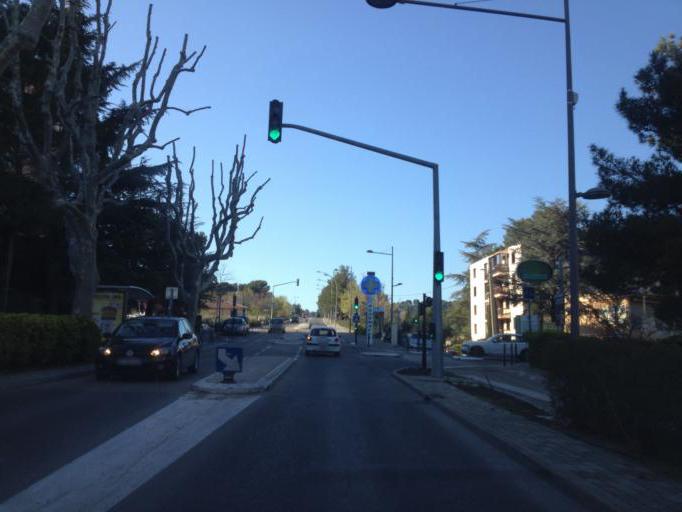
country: FR
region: Provence-Alpes-Cote d'Azur
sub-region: Departement des Bouches-du-Rhone
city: Aix-en-Provence
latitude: 43.5364
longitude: 5.4351
